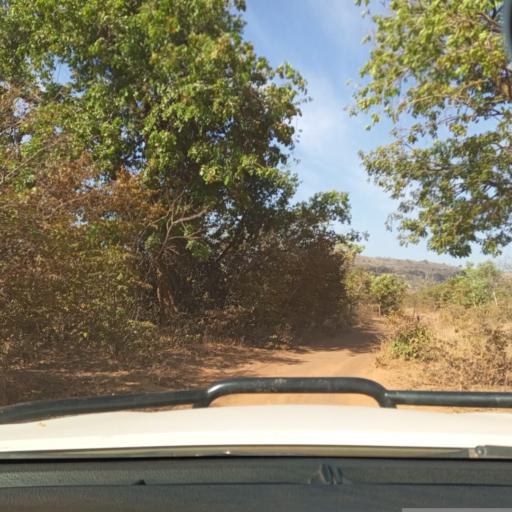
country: ML
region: Bamako
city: Bamako
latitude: 12.5558
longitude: -8.1437
